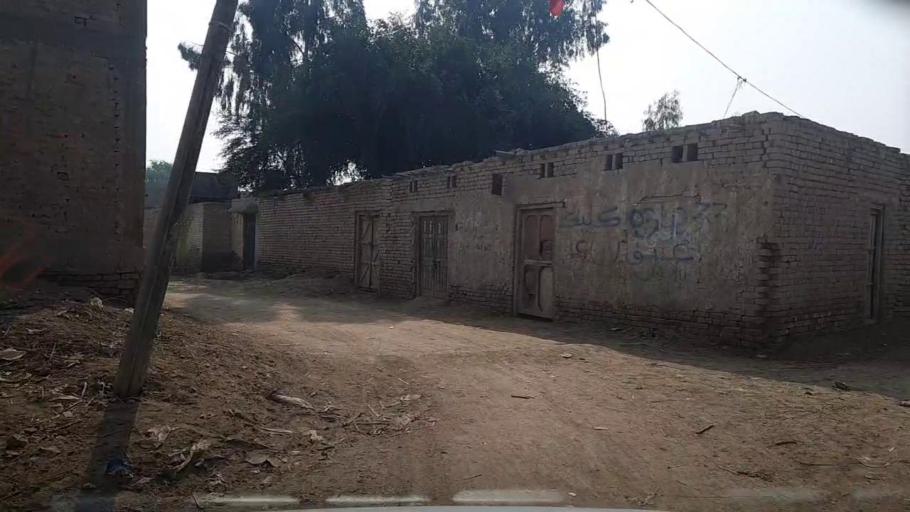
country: PK
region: Sindh
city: Setharja Old
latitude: 27.1394
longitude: 68.5019
